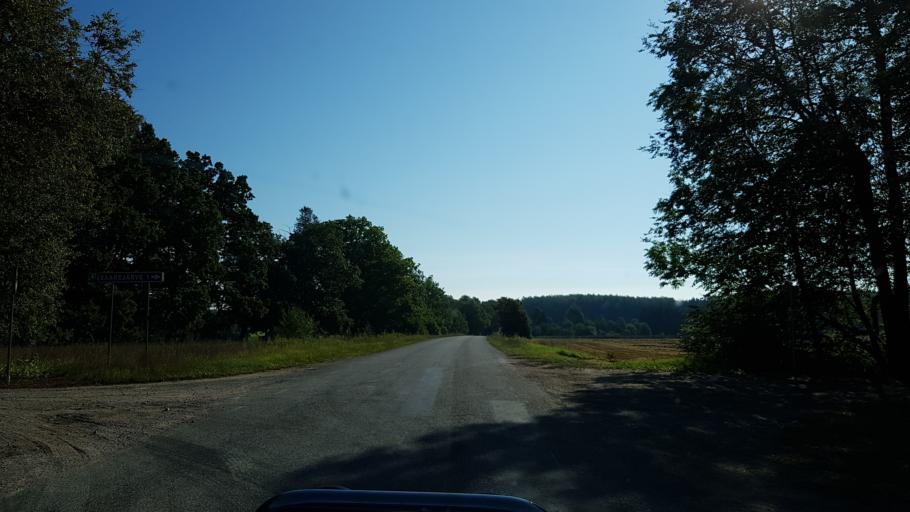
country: EE
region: Jogevamaa
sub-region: Tabivere vald
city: Tabivere
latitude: 58.6695
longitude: 26.7606
